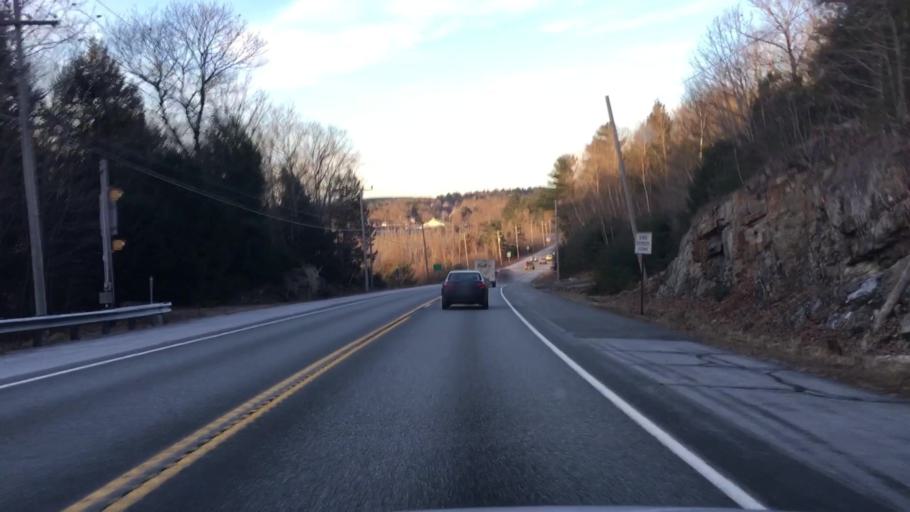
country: US
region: Maine
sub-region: Hancock County
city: Dedham
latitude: 44.7291
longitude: -68.6235
